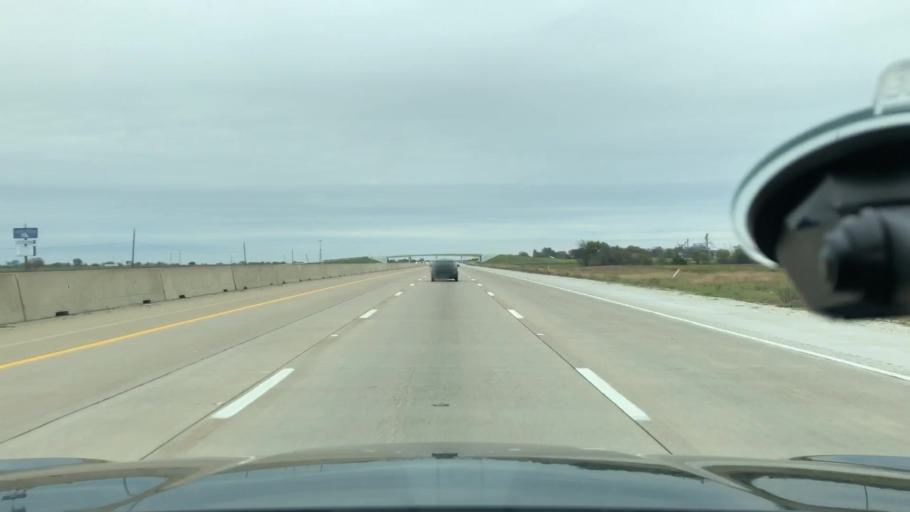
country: US
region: Texas
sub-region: Ellis County
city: Nash
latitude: 32.3168
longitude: -96.8612
